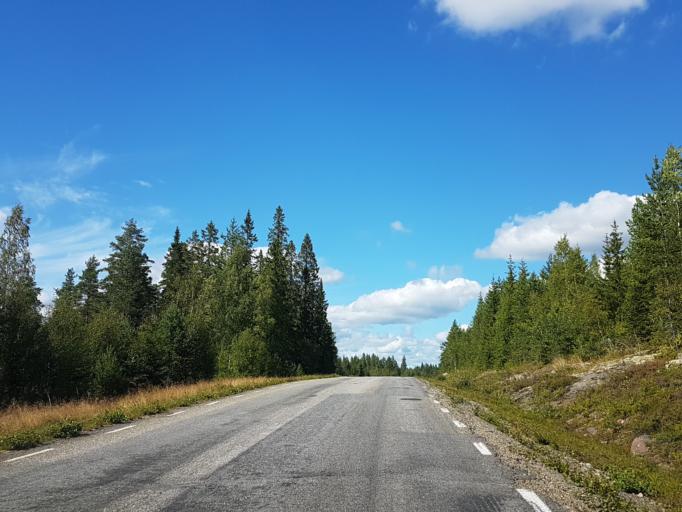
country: SE
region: Vaesterbotten
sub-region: Umea Kommun
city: Saevar
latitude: 64.2255
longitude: 20.4679
